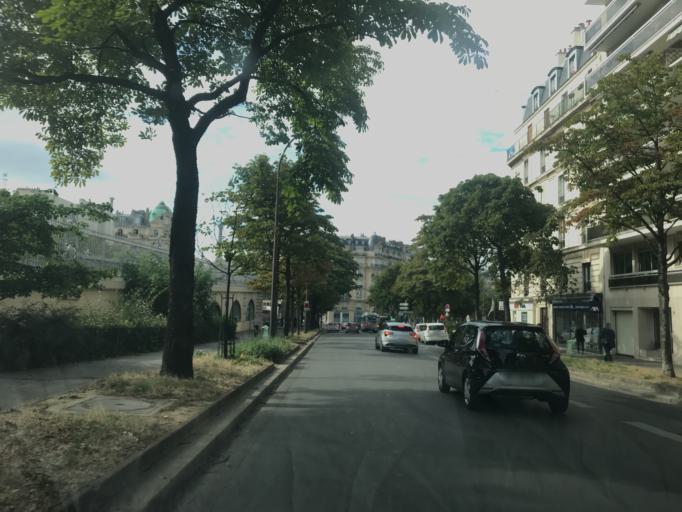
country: FR
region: Ile-de-France
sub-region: Departement des Hauts-de-Seine
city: Malakoff
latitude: 48.8438
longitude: 2.3121
